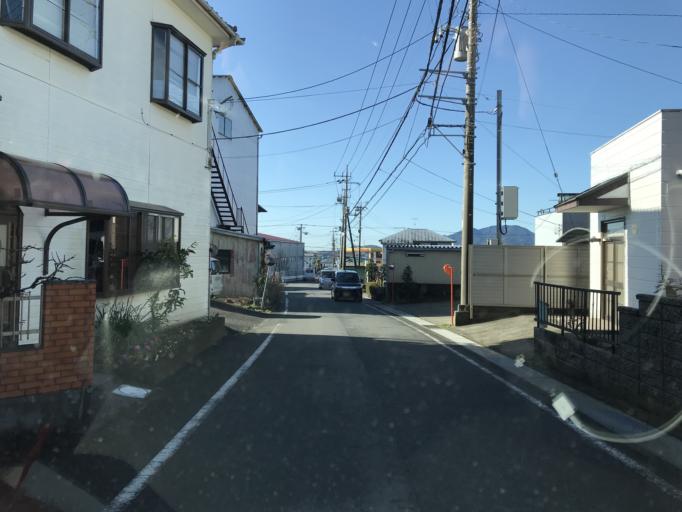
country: JP
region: Shizuoka
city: Fujinomiya
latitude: 35.2210
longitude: 138.6455
